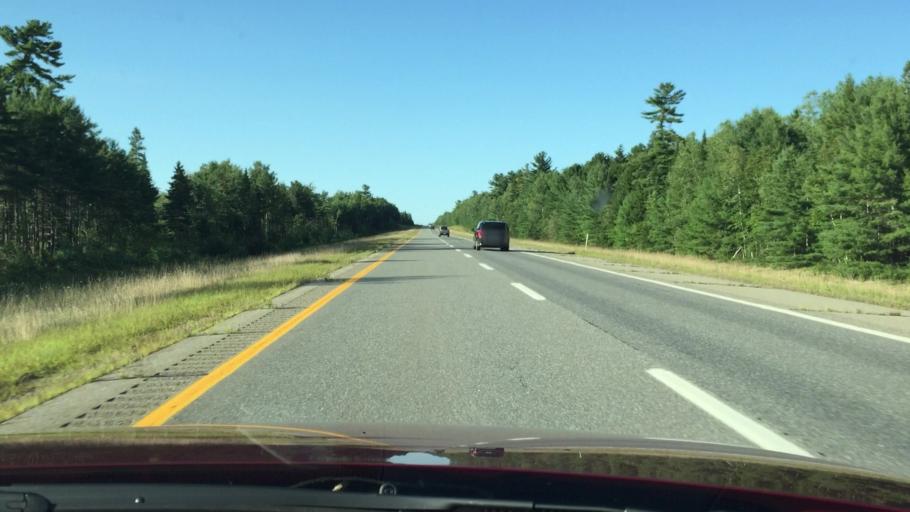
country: US
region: Maine
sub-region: Penobscot County
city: Lincoln
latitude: 45.4024
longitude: -68.5976
